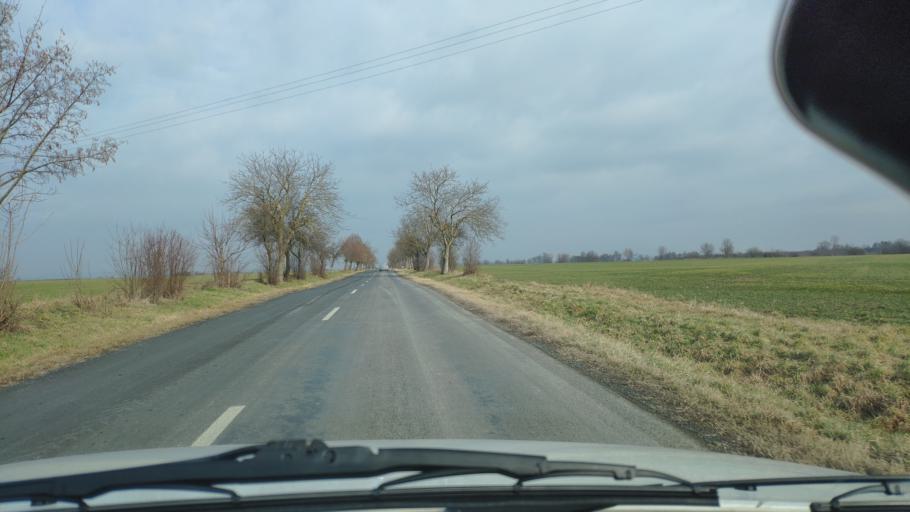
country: HU
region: Zala
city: Murakeresztur
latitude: 46.4361
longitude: 16.9097
